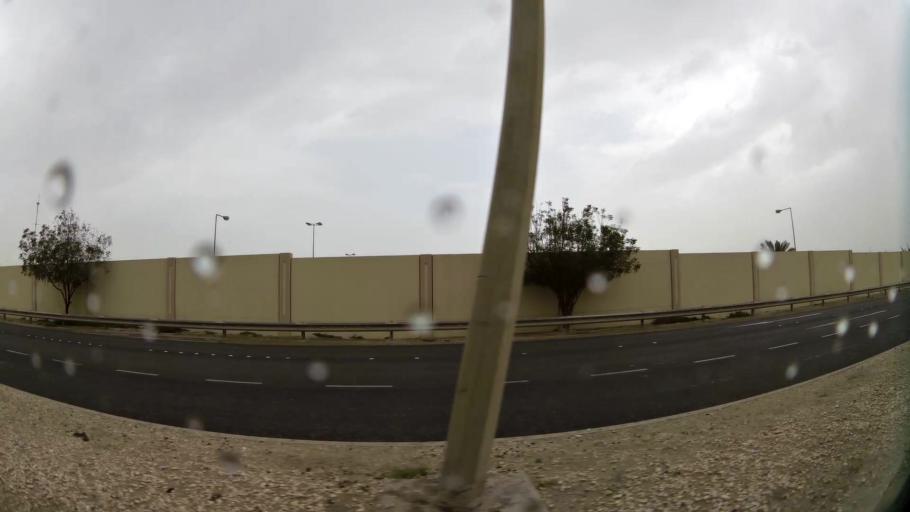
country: BH
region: Northern
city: Ar Rifa'
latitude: 26.1405
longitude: 50.5527
